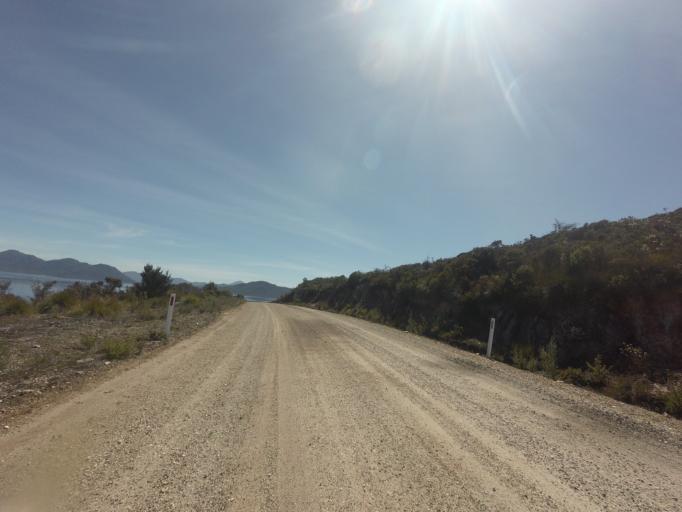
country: AU
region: Tasmania
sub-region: Huon Valley
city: Geeveston
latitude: -43.0308
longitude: 146.3412
